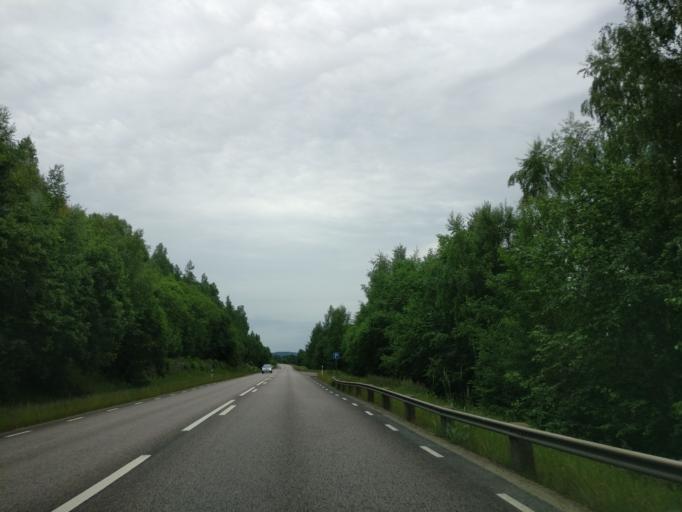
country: SE
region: Vaermland
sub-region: Hagfors Kommun
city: Hagfors
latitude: 60.0338
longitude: 13.6036
